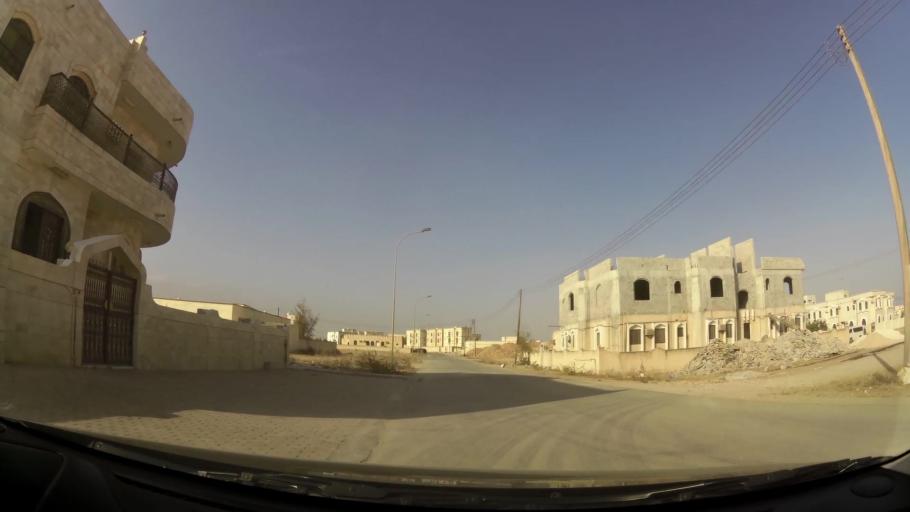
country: OM
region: Zufar
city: Salalah
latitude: 17.0218
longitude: 54.0205
